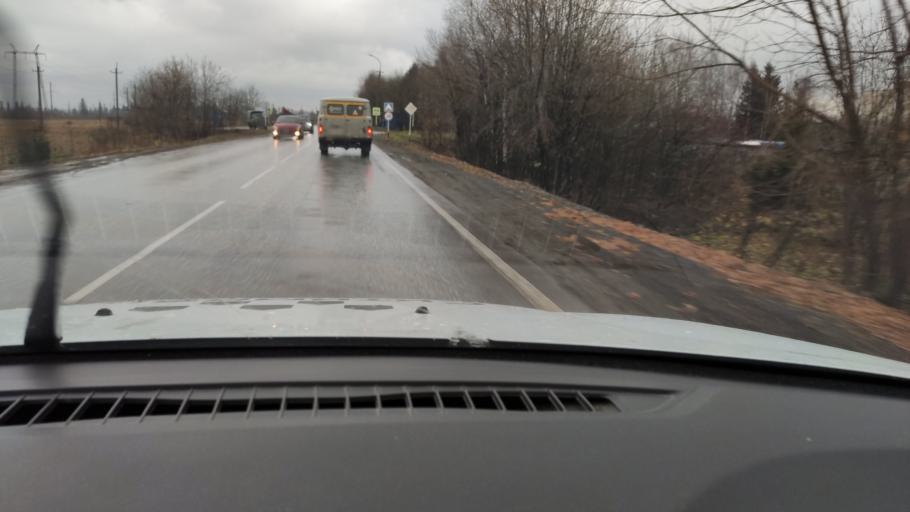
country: RU
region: Perm
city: Sylva
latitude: 58.0281
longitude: 56.7134
